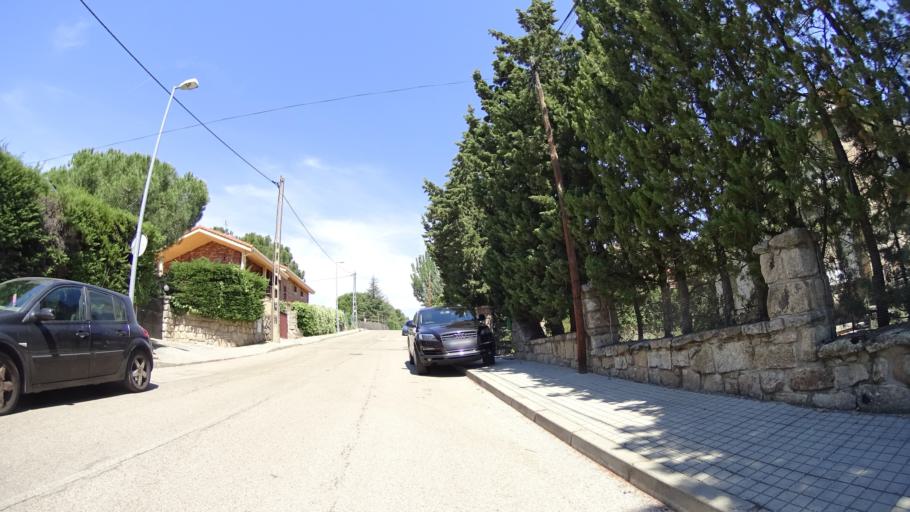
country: ES
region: Madrid
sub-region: Provincia de Madrid
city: Colmenarejo
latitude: 40.5549
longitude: -4.0053
